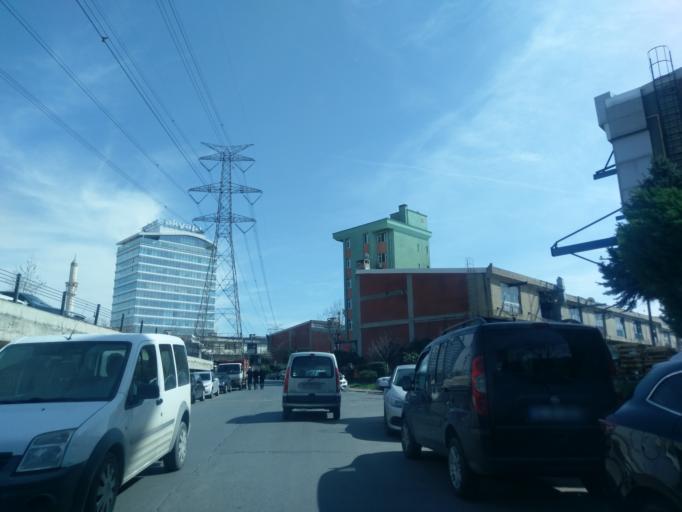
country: TR
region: Istanbul
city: Basaksehir
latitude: 41.0695
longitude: 28.8012
